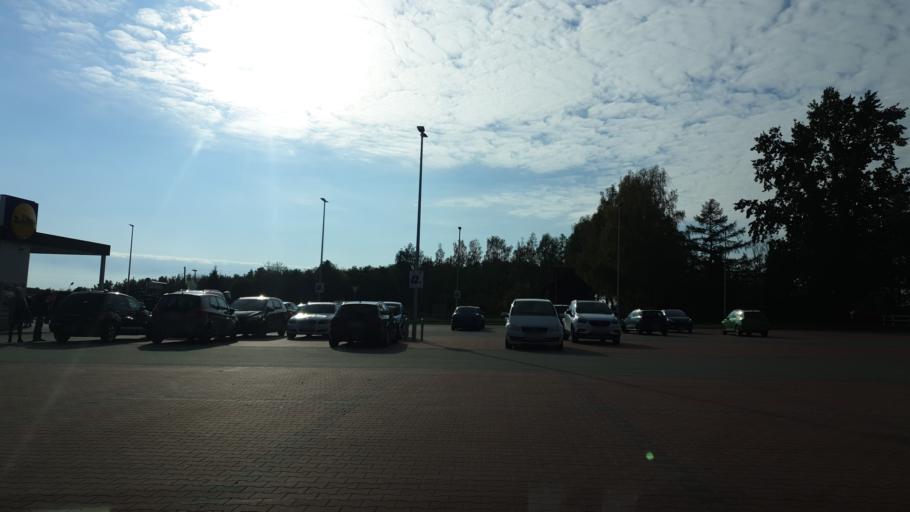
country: DE
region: Saxony
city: Meerane
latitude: 50.8435
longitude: 12.4445
